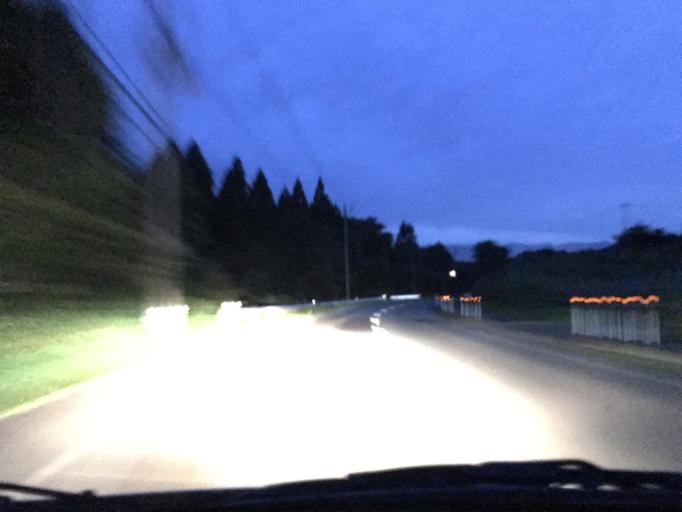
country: JP
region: Iwate
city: Kitakami
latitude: 39.2895
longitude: 141.1501
